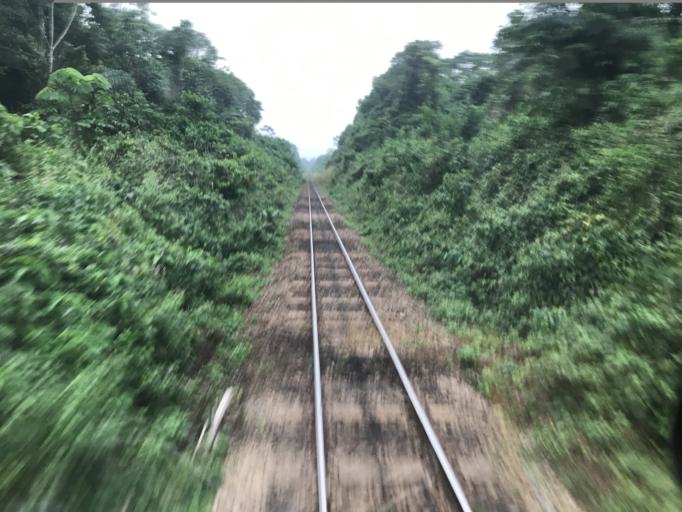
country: CM
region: Littoral
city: Edea
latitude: 3.9354
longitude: 10.1004
